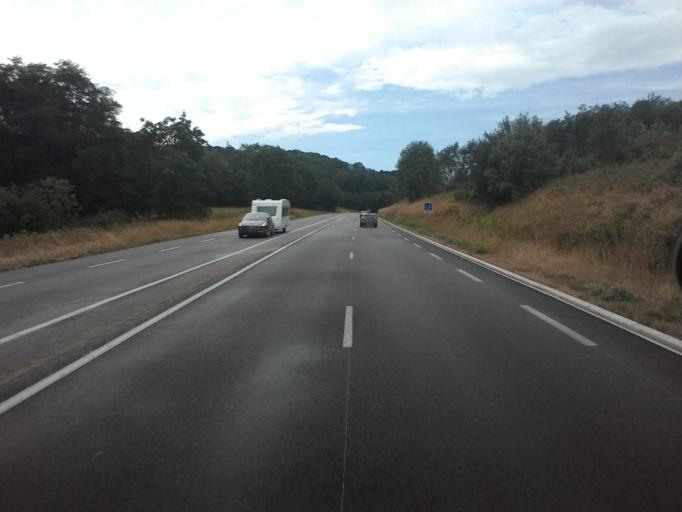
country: FR
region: Franche-Comte
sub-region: Departement du Jura
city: Bletterans
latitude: 46.7979
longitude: 5.5709
